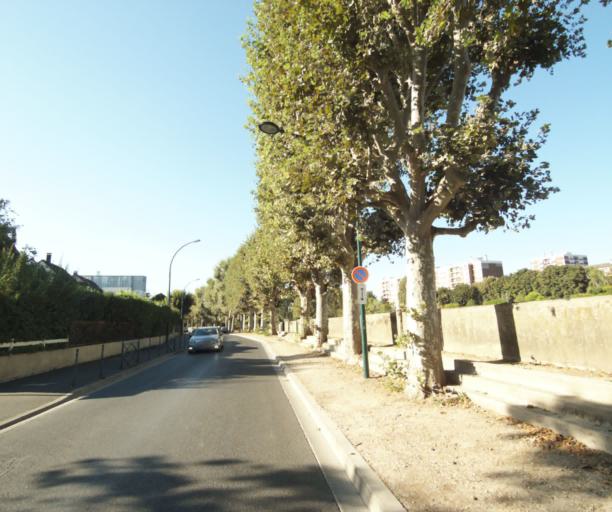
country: FR
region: Ile-de-France
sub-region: Departement de Seine-Saint-Denis
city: Villetaneuse
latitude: 48.9399
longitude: 2.3352
